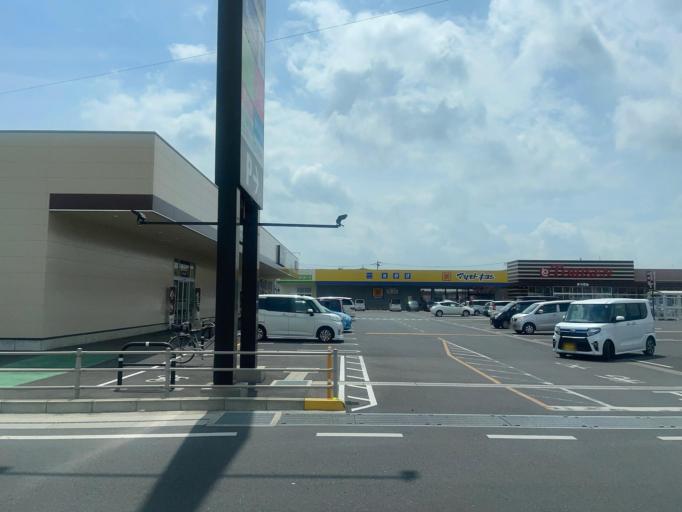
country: JP
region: Tochigi
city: Tochigi
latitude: 36.3788
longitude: 139.7264
